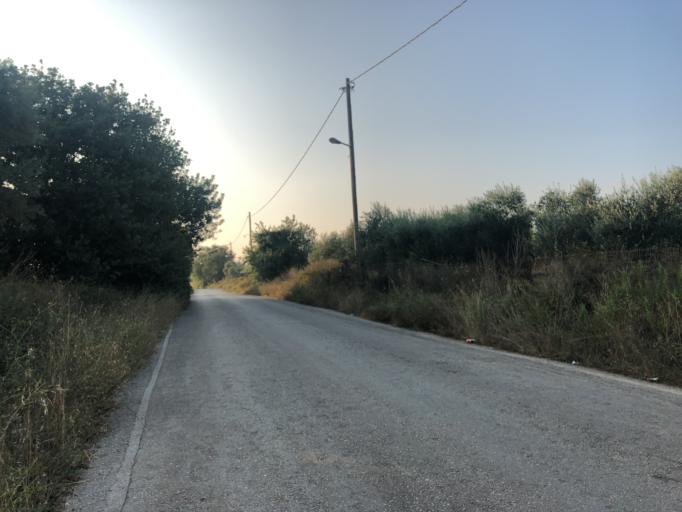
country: GR
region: Crete
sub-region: Nomos Chanias
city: Georgioupolis
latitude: 35.3509
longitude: 24.2775
